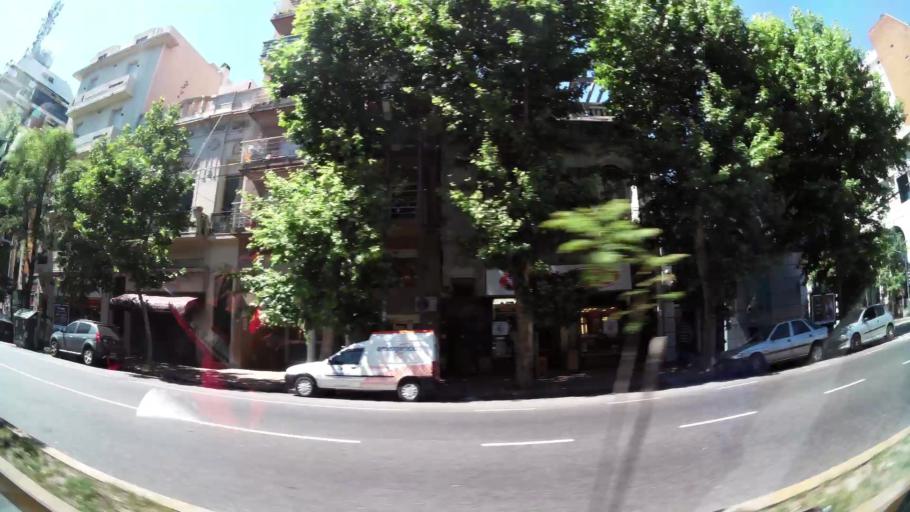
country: AR
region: Buenos Aires F.D.
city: Buenos Aires
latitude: -34.6368
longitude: -58.4037
